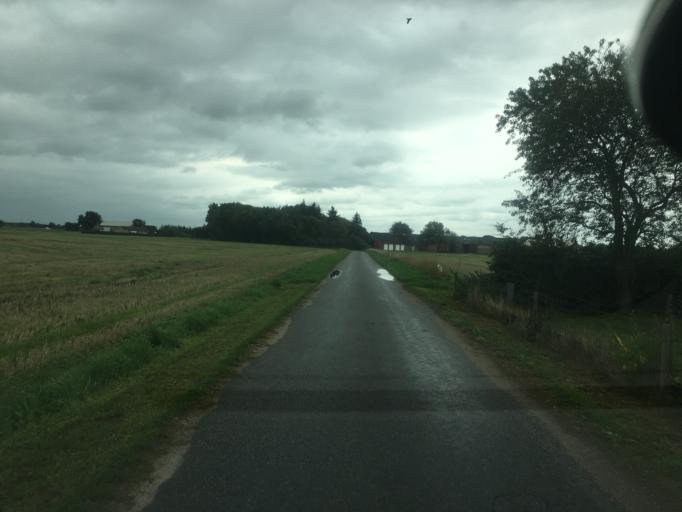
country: DK
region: South Denmark
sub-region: Tonder Kommune
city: Tonder
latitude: 54.9647
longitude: 8.9288
